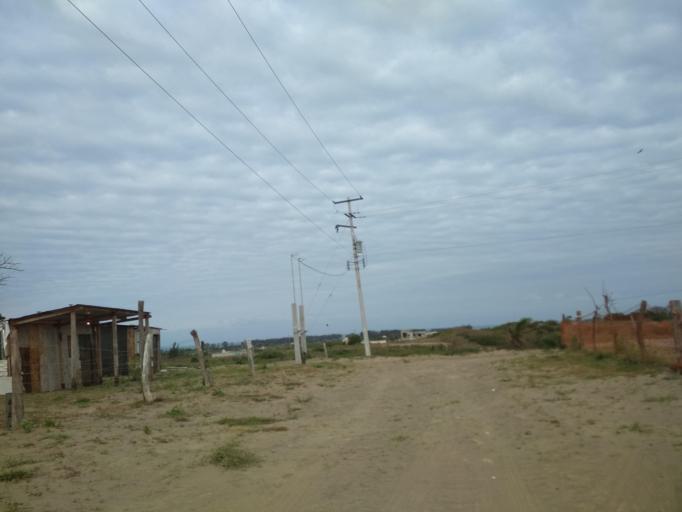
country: MX
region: Veracruz
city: Anton Lizardo
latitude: 19.0454
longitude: -95.9918
